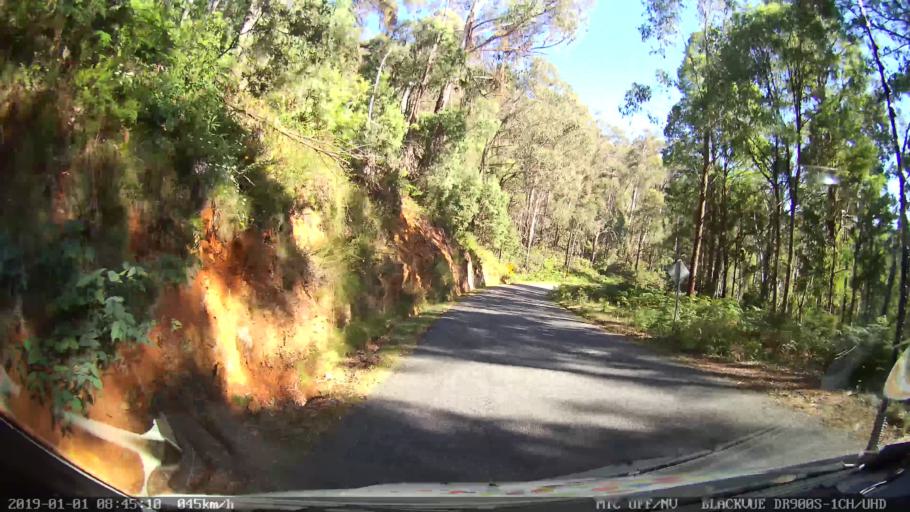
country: AU
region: New South Wales
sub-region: Snowy River
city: Jindabyne
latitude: -36.3071
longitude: 148.1878
